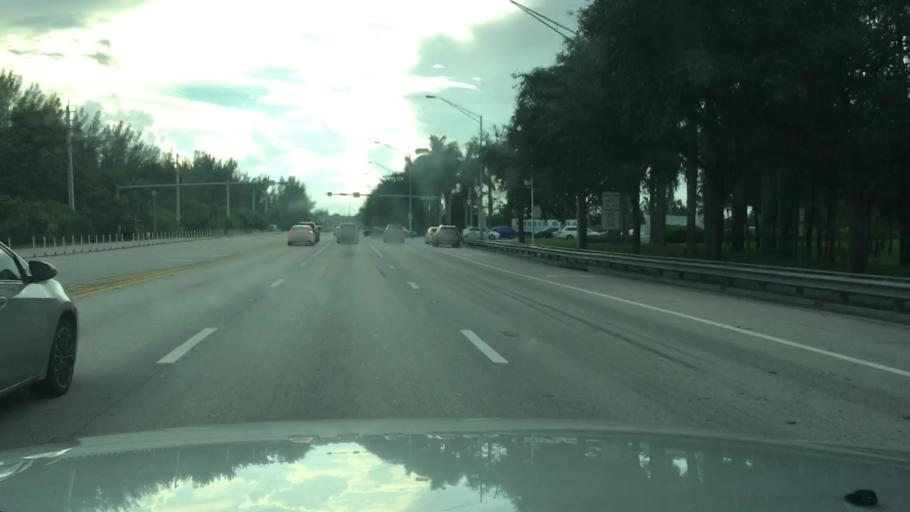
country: US
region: Florida
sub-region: Miami-Dade County
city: Sweetwater
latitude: 25.7819
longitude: -80.3788
